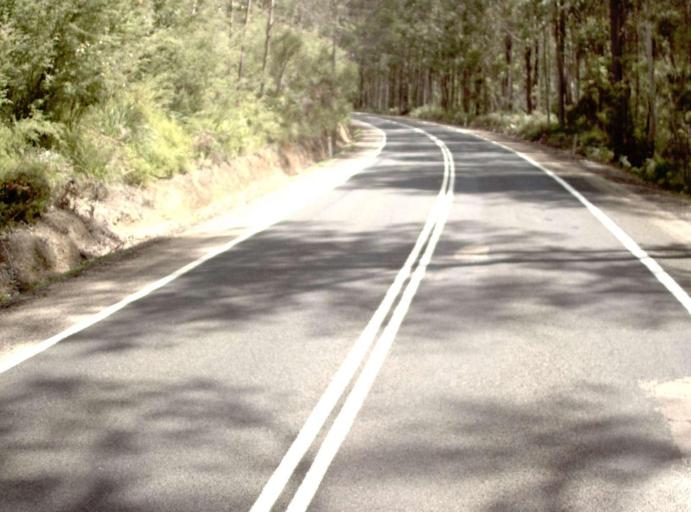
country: AU
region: New South Wales
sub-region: Bombala
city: Bombala
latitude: -37.5372
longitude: 149.3688
